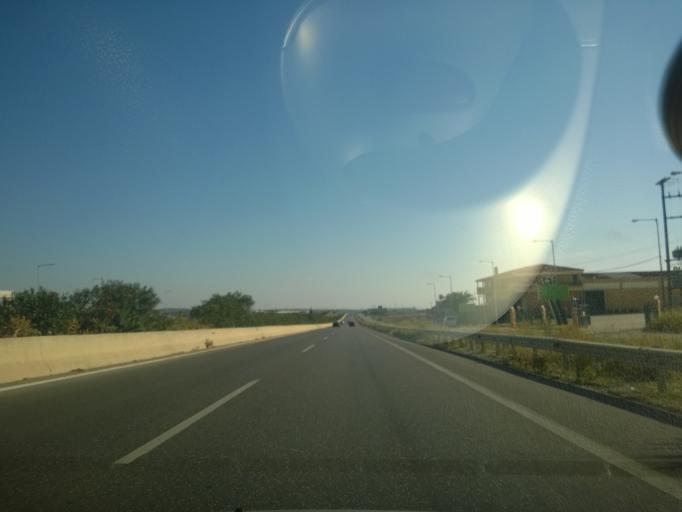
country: GR
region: Central Macedonia
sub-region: Nomos Chalkidikis
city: Lakkoma
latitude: 40.3841
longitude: 23.0386
